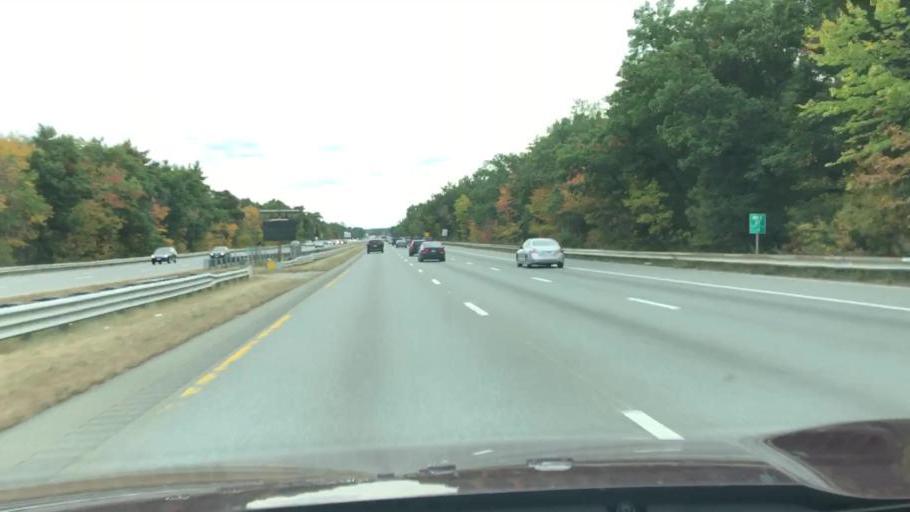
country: US
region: Massachusetts
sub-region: Essex County
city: Andover
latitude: 42.6214
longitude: -71.1770
